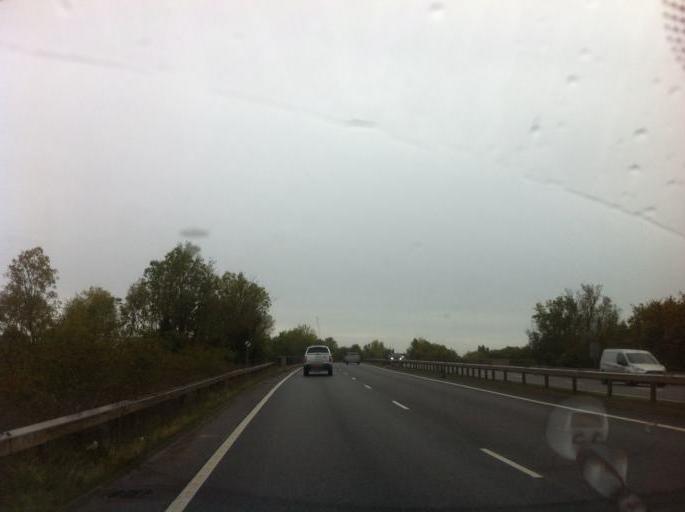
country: GB
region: England
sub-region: Peterborough
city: Peterborough
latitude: 52.5573
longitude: -0.2306
